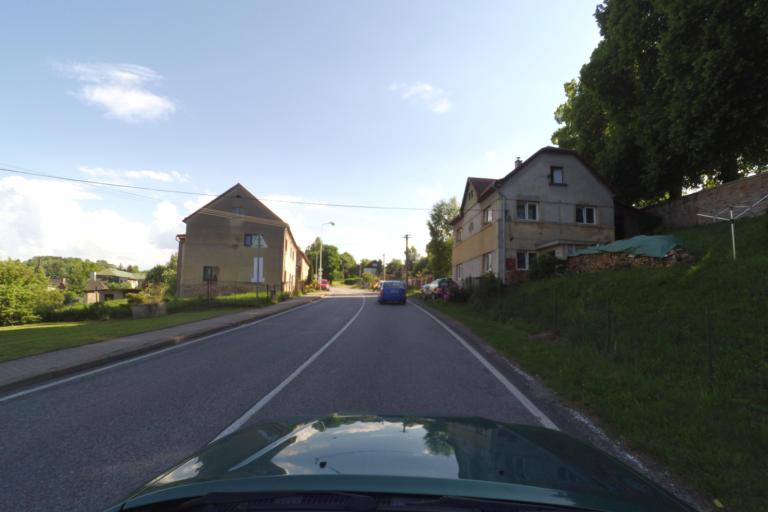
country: CZ
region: Kralovehradecky
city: Zacler
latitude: 50.6452
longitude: 15.9649
